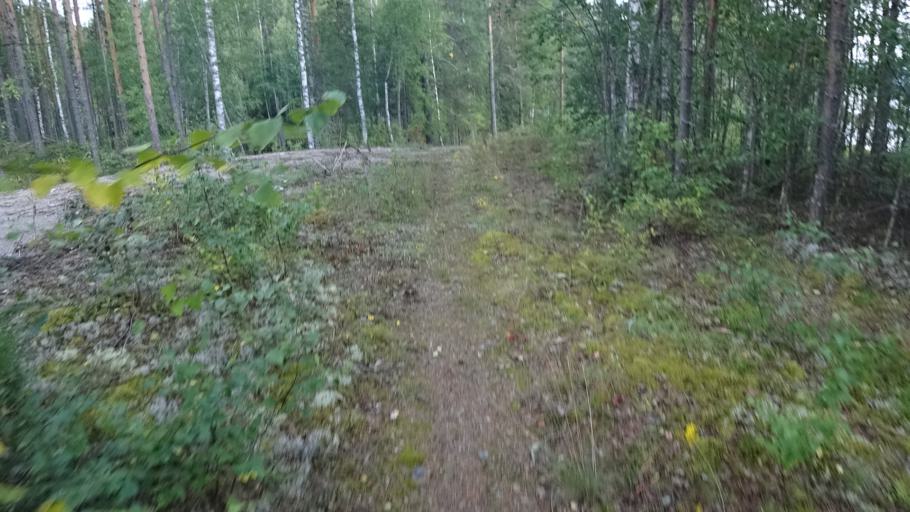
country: FI
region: North Karelia
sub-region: Joensuu
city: Ilomantsi
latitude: 62.6219
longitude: 31.1937
